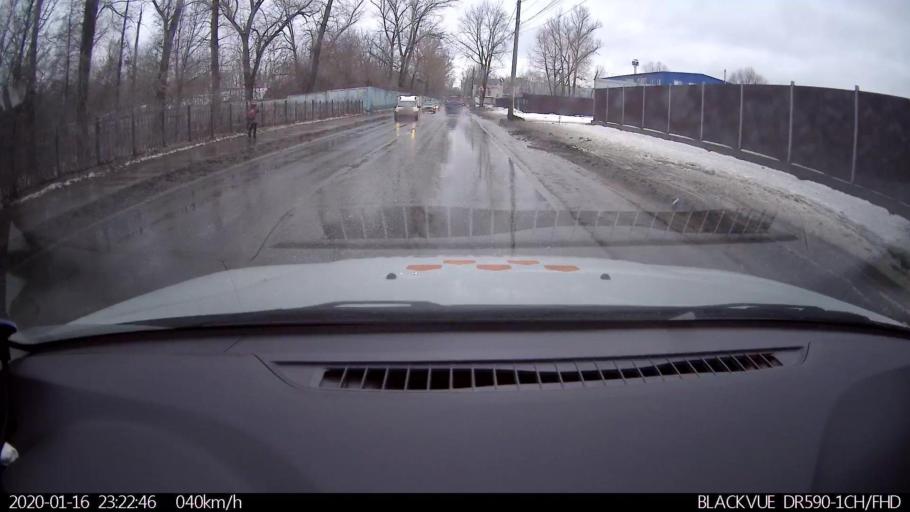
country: RU
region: Nizjnij Novgorod
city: Nizhniy Novgorod
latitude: 56.2959
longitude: 43.9115
